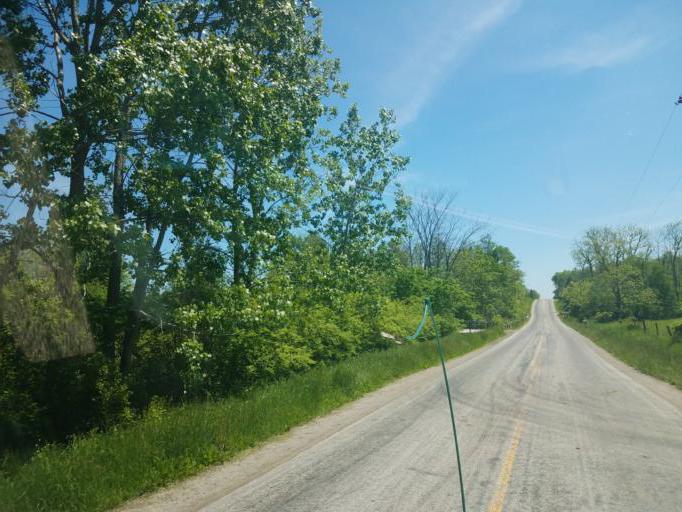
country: US
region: Ohio
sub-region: Wayne County
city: West Salem
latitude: 40.9447
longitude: -82.1887
